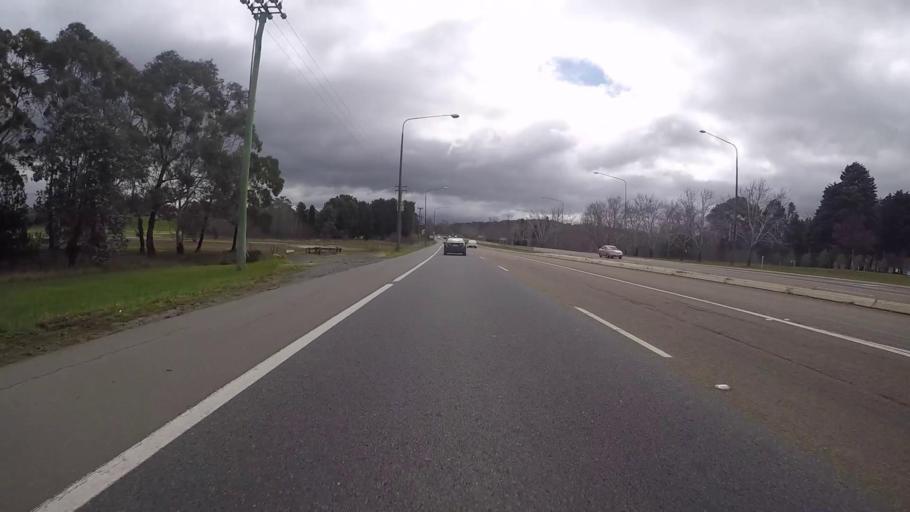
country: AU
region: Australian Capital Territory
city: Kaleen
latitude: -35.2196
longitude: 149.1188
